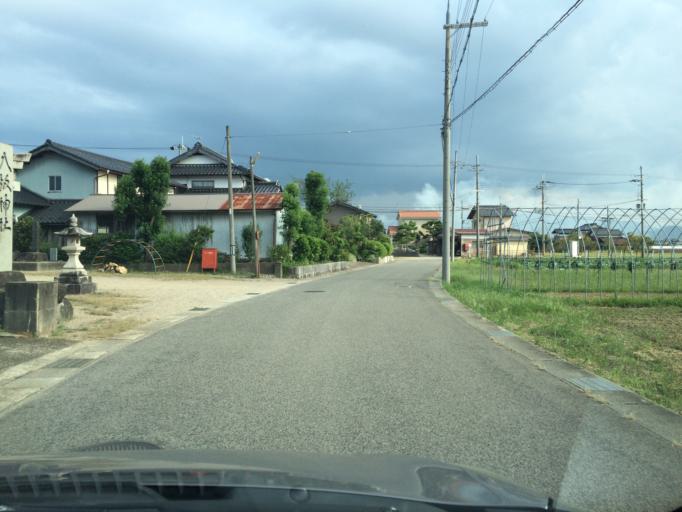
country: JP
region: Hyogo
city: Toyooka
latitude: 35.5233
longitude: 134.8270
